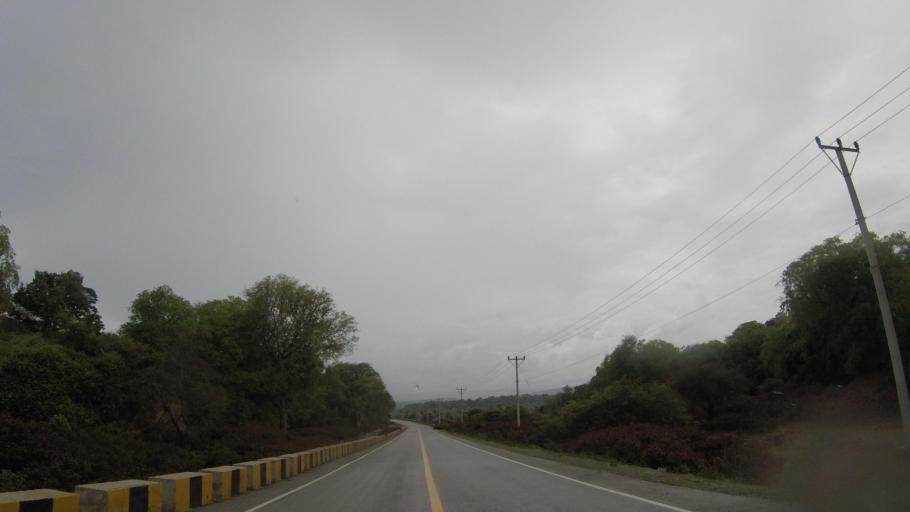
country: TL
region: Lautem
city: Lospalos
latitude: -8.4034
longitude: 126.8260
